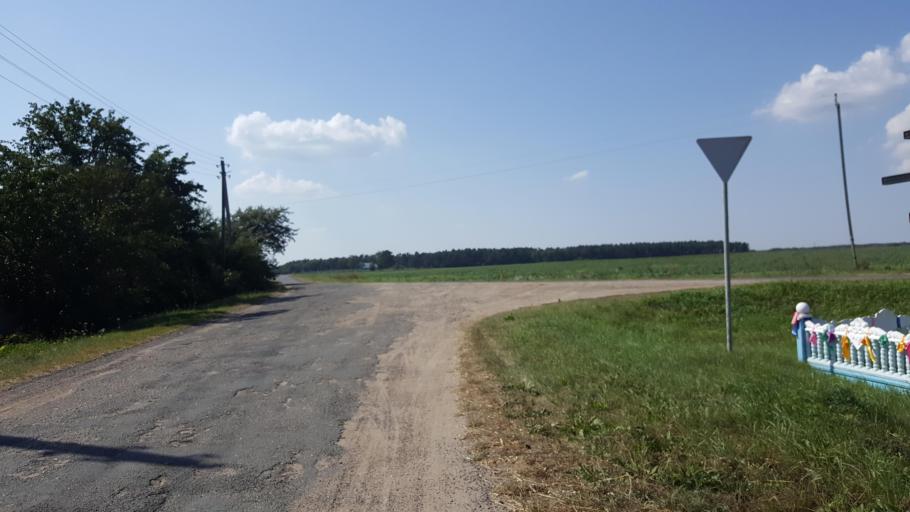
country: PL
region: Podlasie
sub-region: Powiat hajnowski
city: Czeremcha
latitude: 52.4791
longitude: 23.5307
